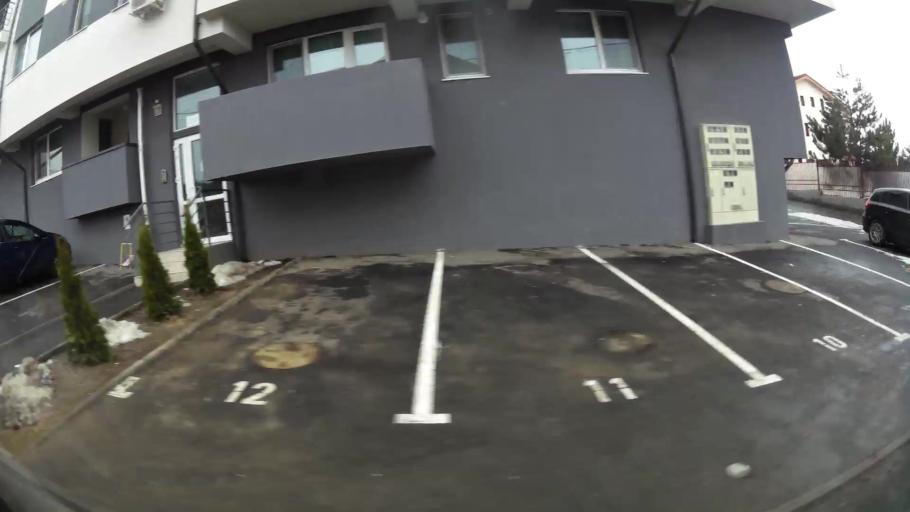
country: RO
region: Ilfov
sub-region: Comuna Popesti-Leordeni
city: Popesti-Leordeni
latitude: 44.4030
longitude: 26.1724
